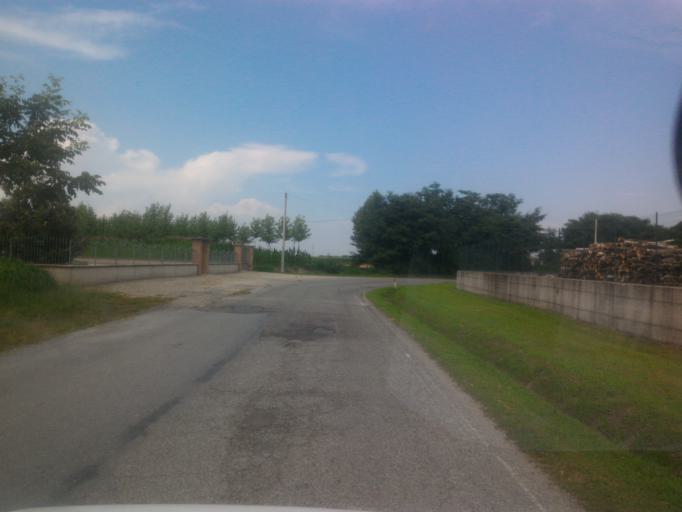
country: IT
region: Piedmont
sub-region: Provincia di Torino
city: Vigone
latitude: 44.8429
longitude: 7.4787
